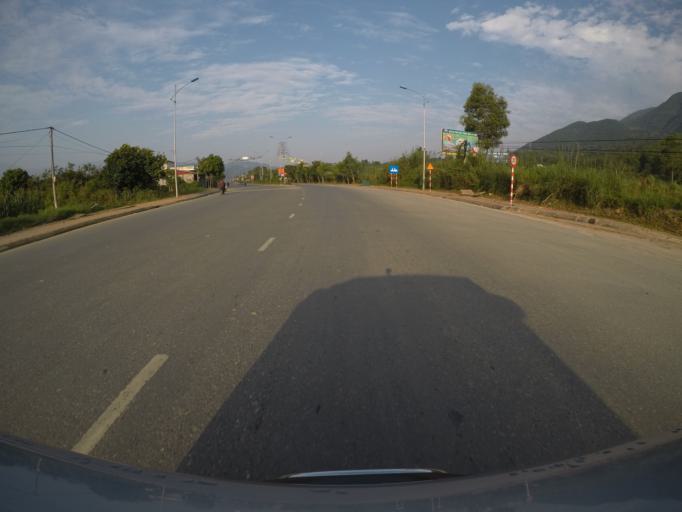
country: VN
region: Lai Chau
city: Tam Duong
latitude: 22.3198
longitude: 103.6368
